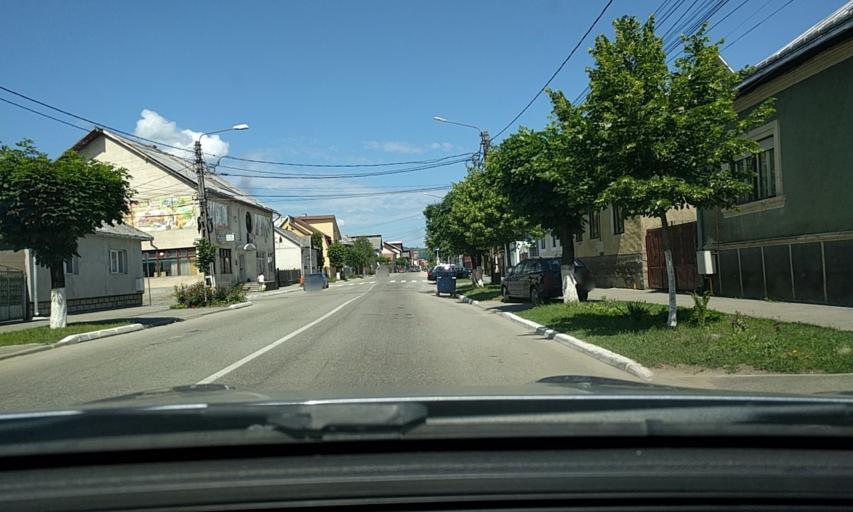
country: RO
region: Bistrita-Nasaud
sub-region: Oras Nasaud
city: Nasaud
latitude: 47.2886
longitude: 24.3936
